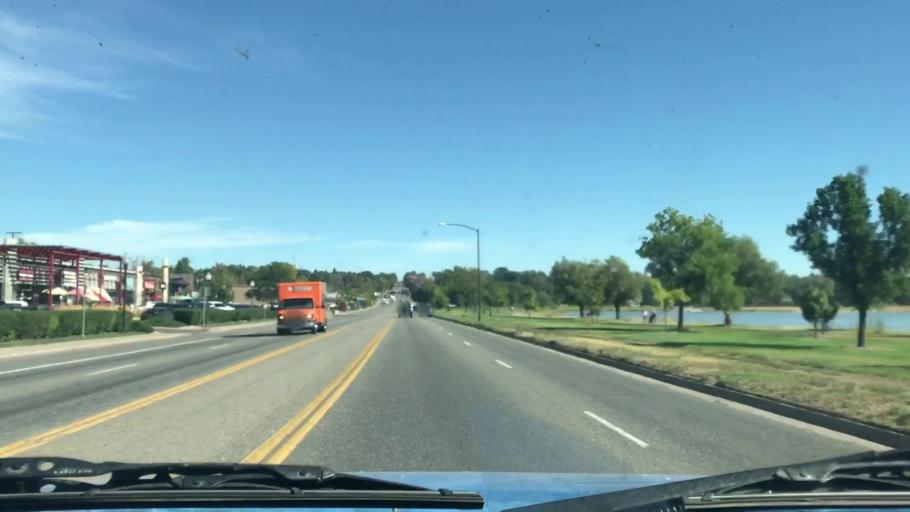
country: US
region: Colorado
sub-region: Jefferson County
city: Edgewater
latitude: 39.7475
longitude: -105.0532
